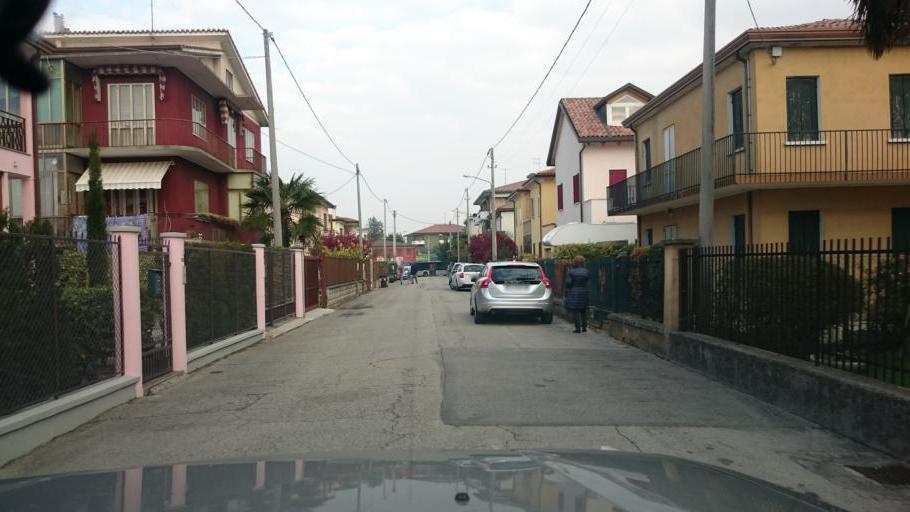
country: IT
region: Veneto
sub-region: Provincia di Padova
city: Tencarola
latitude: 45.3949
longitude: 11.8285
